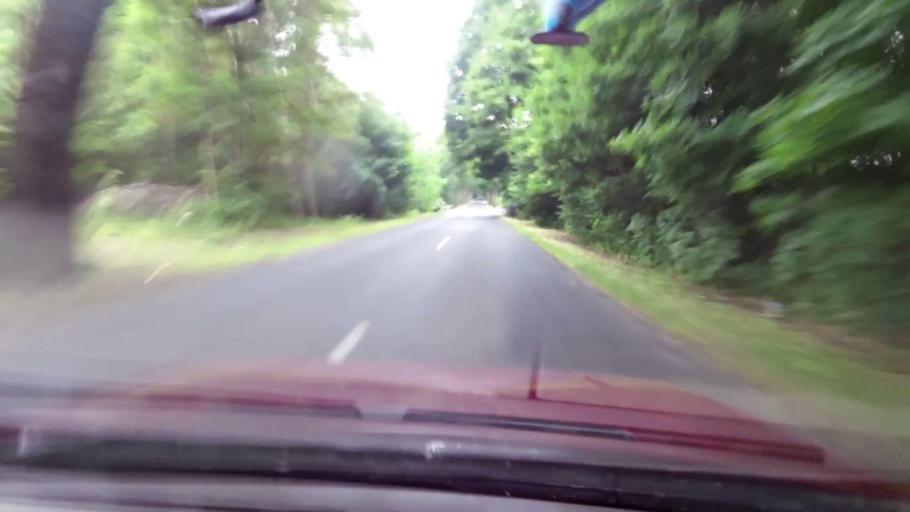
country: PL
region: West Pomeranian Voivodeship
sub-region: Powiat koszalinski
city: Polanow
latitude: 54.1378
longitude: 16.5124
